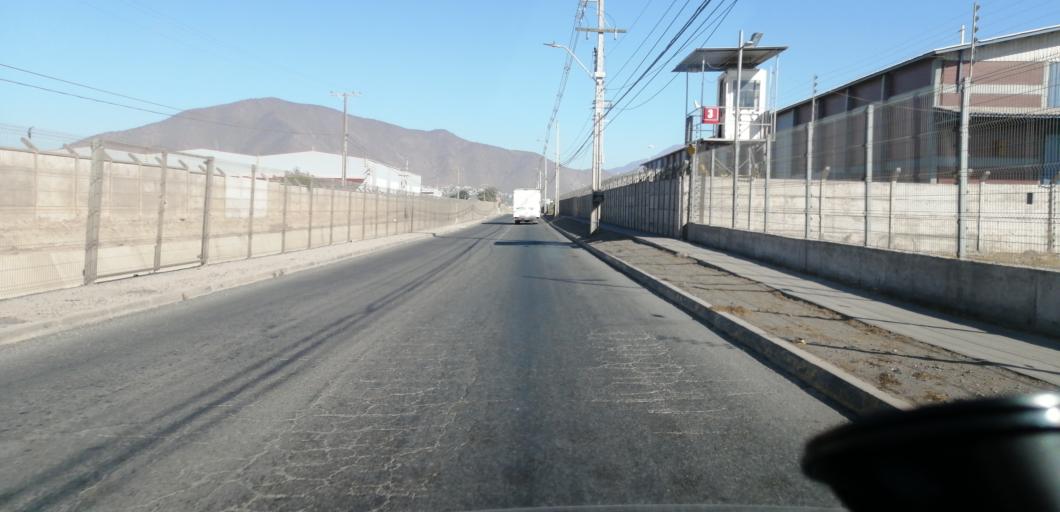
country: CL
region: Santiago Metropolitan
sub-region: Provincia de Santiago
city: Lo Prado
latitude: -33.4574
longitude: -70.7840
